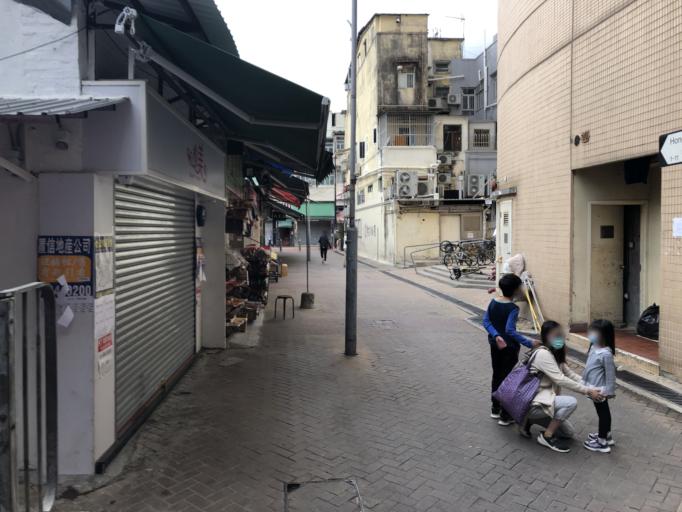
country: HK
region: Tai Po
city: Tai Po
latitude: 22.5049
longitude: 114.1285
